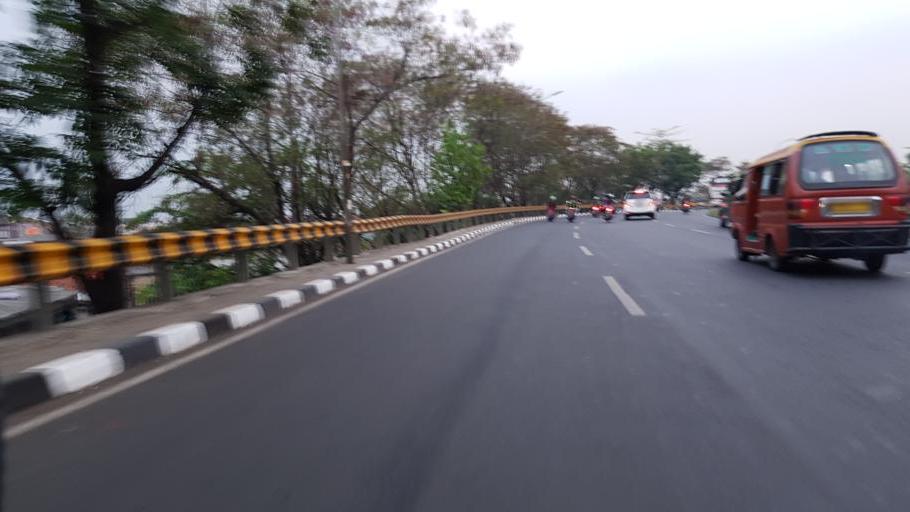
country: ID
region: Jakarta Raya
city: Jakarta
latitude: -6.3070
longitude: 106.8862
